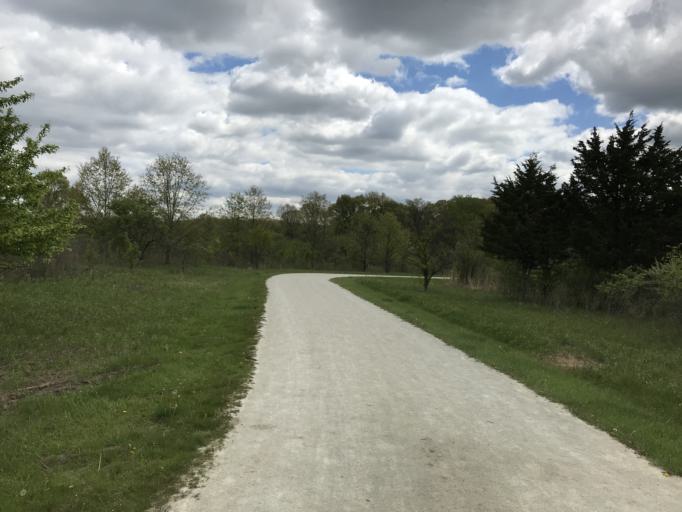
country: US
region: Illinois
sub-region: DuPage County
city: Woodridge
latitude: 41.7355
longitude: -88.0856
